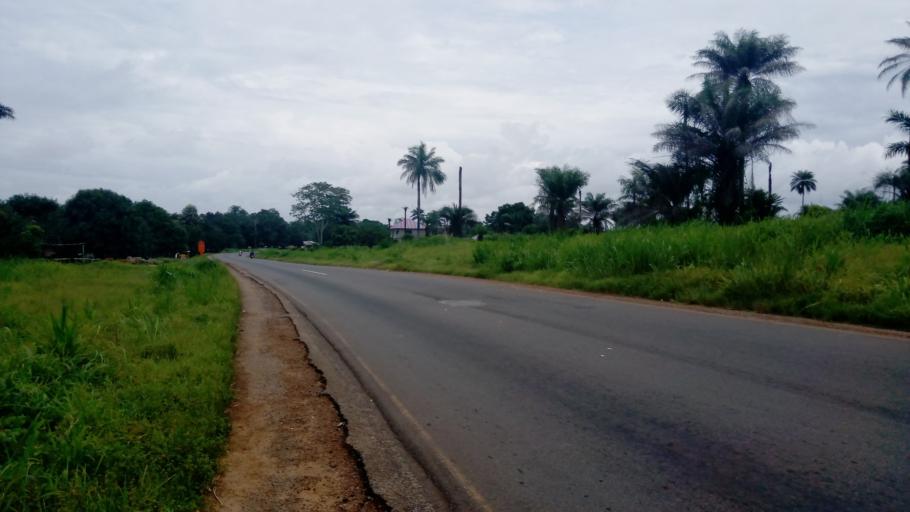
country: SL
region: Northern Province
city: Port Loko
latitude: 8.5036
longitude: -12.7591
